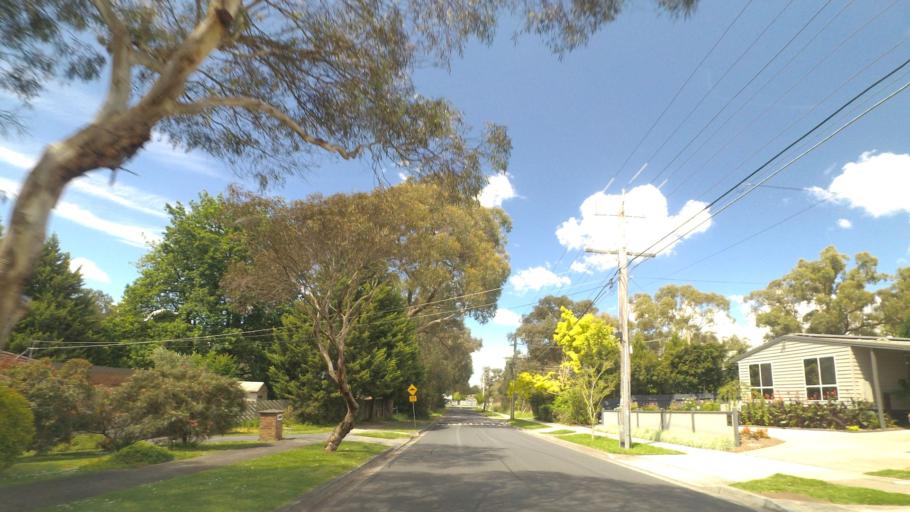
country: AU
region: Victoria
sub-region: Maroondah
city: Croydon South
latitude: -37.8221
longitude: 145.2750
